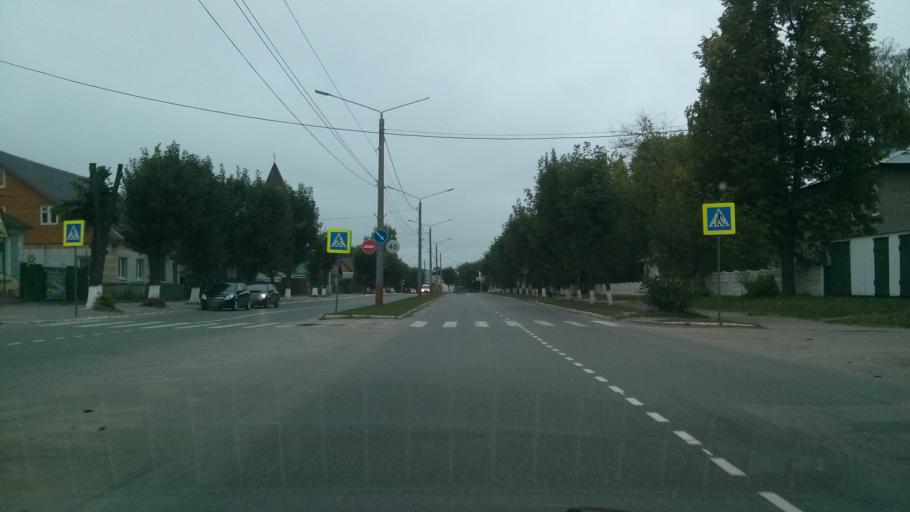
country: RU
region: Vladimir
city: Murom
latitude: 55.5817
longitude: 42.0364
